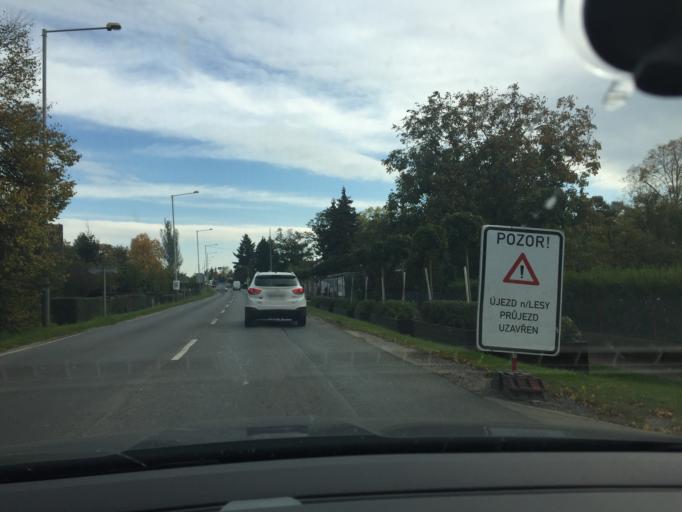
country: CZ
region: Praha
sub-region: Praha 20
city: Horni Pocernice
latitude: 50.0807
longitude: 14.6189
